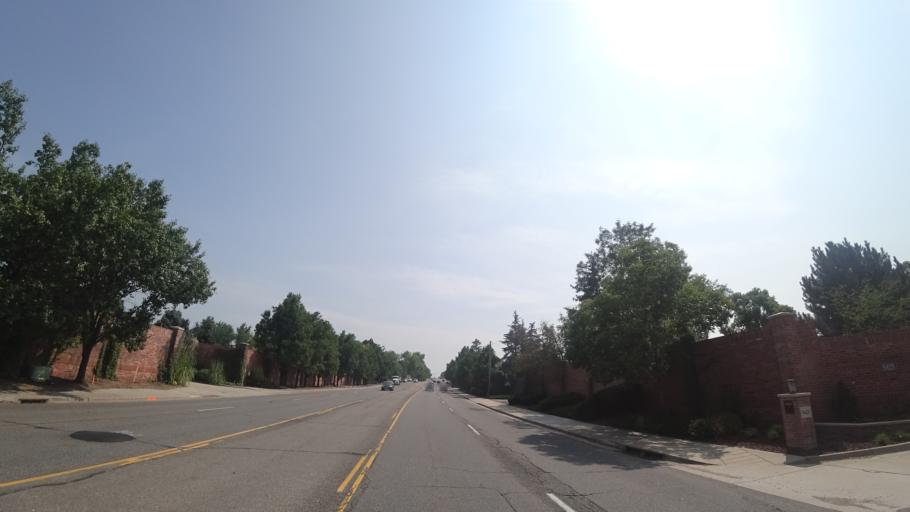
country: US
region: Colorado
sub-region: Arapahoe County
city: Greenwood Village
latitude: 39.6187
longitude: -104.9599
